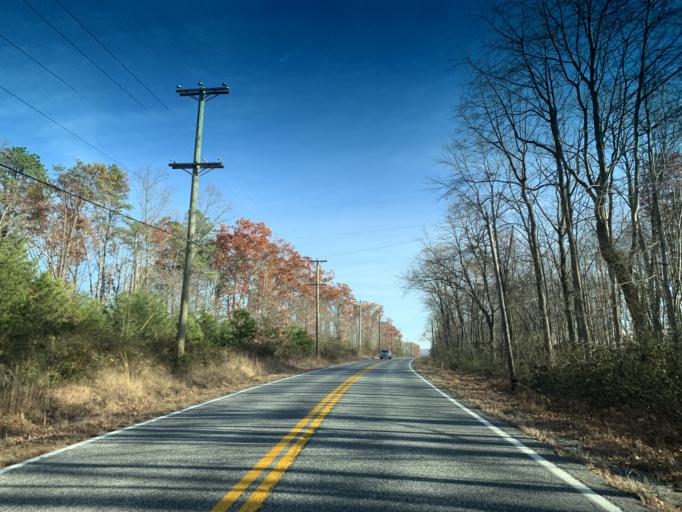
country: US
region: Maryland
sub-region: Cecil County
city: Charlestown
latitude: 39.5832
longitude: -76.0096
